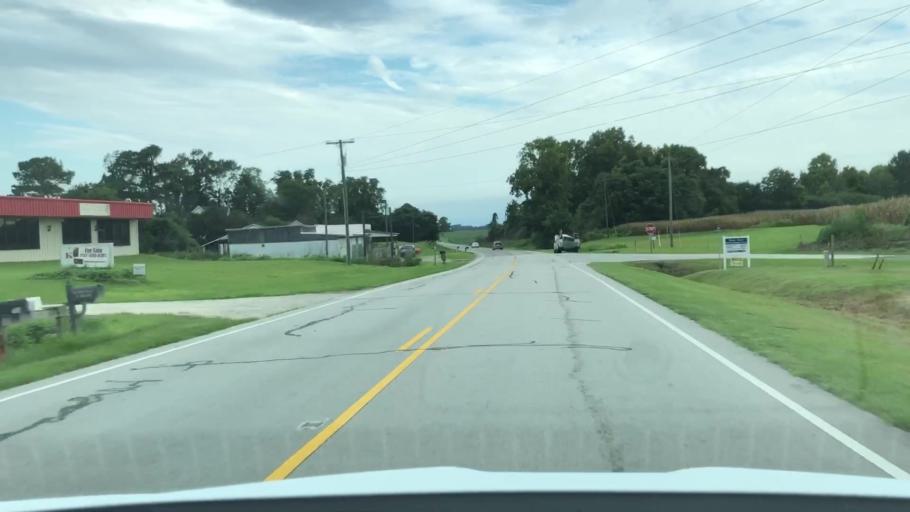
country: US
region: North Carolina
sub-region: Lenoir County
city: Kinston
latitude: 35.1377
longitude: -77.5291
